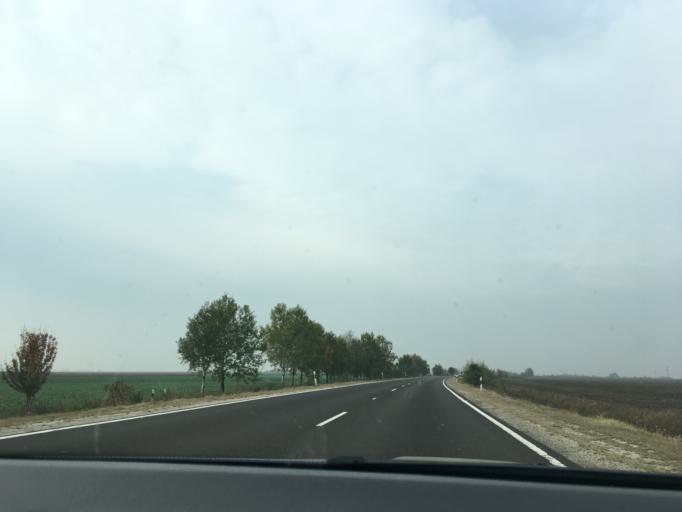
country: HU
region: Pest
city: Abony
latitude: 47.1967
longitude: 20.0815
